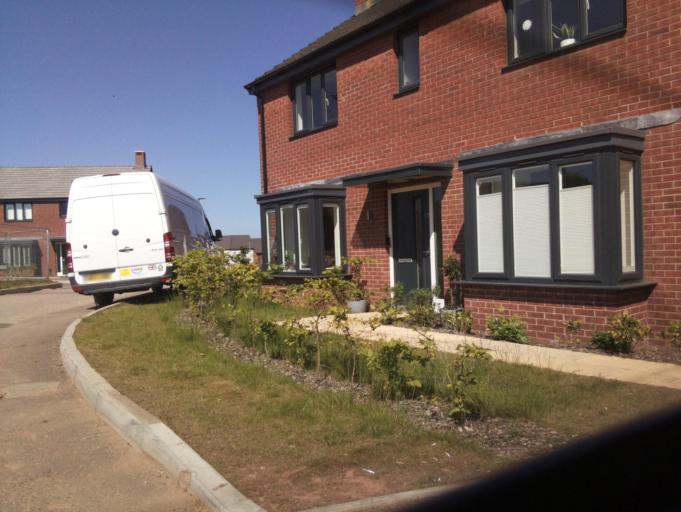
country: GB
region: England
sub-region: Borough of Torbay
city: Paignton
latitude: 50.4112
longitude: -3.5839
